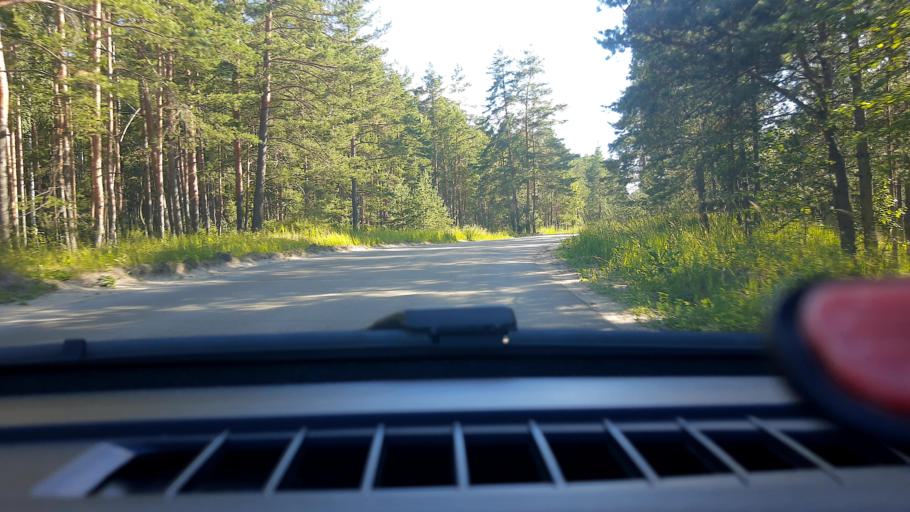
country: RU
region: Nizjnij Novgorod
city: Babino
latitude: 56.3241
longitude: 43.6343
